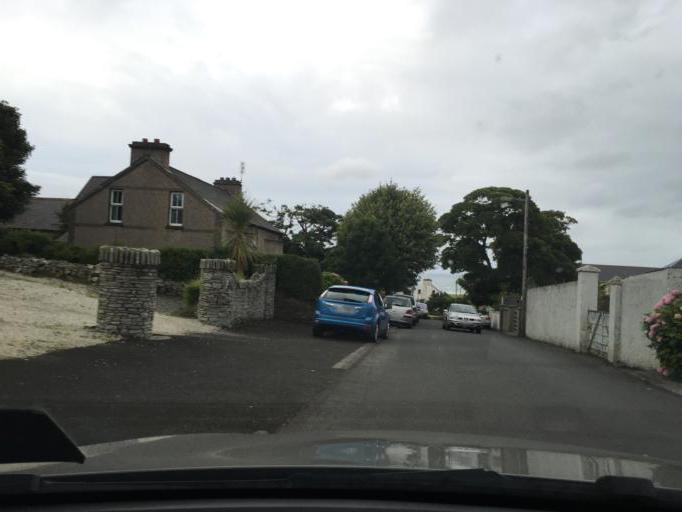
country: IE
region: Ulster
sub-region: County Donegal
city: Carndonagh
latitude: 55.2798
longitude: -7.3940
